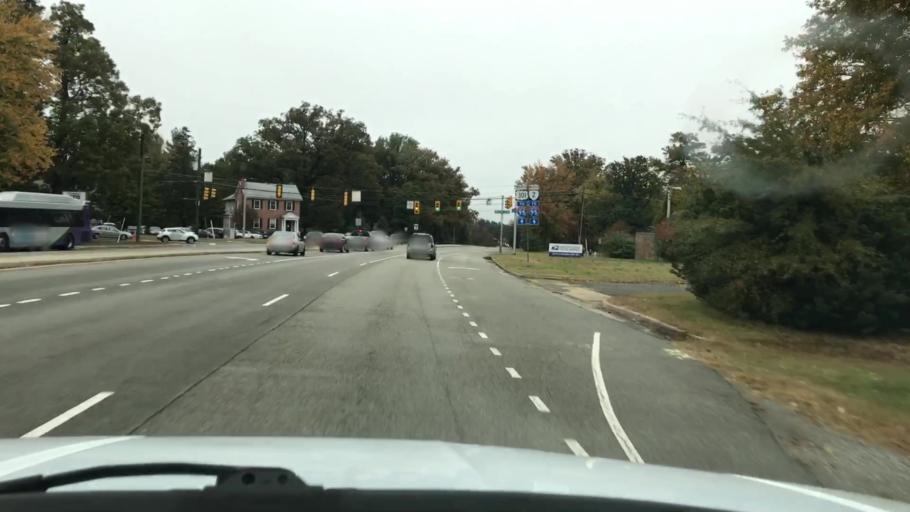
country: US
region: Virginia
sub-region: Henrico County
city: Lakeside
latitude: 37.6049
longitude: -77.4502
